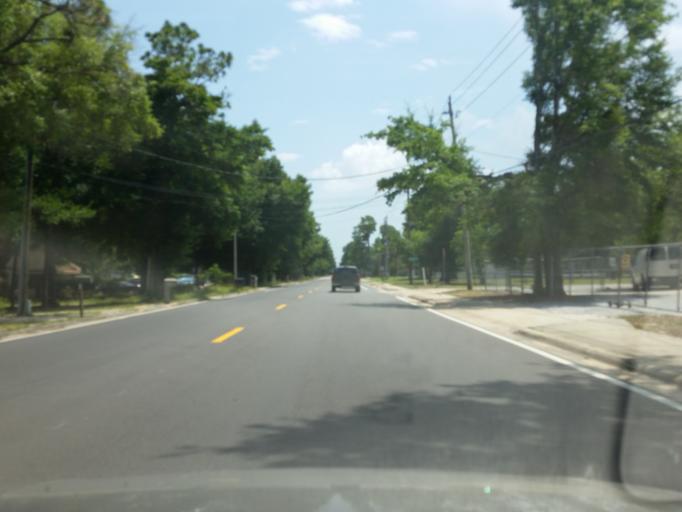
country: US
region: Florida
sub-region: Escambia County
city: Ferry Pass
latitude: 30.4942
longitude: -87.1666
